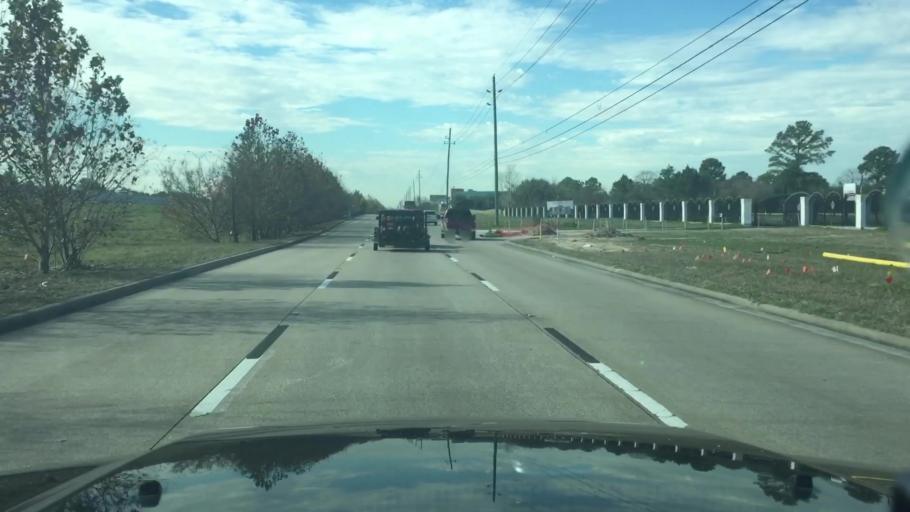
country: US
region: Texas
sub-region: Harris County
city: Hudson
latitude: 29.9350
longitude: -95.5327
